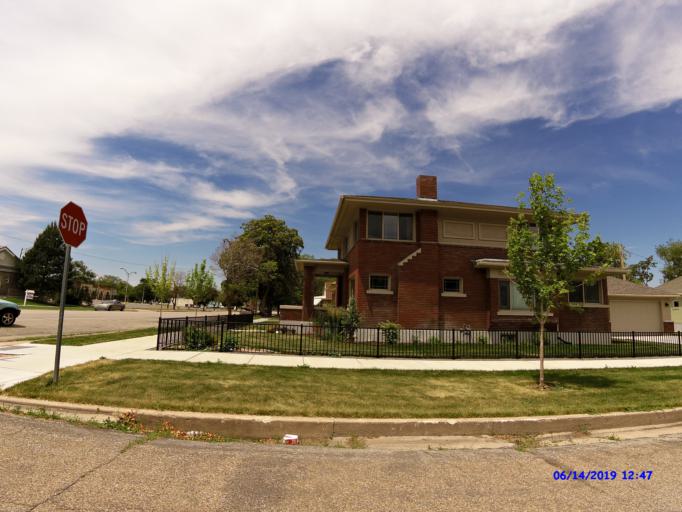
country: US
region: Utah
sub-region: Weber County
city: Ogden
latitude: 41.2227
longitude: -111.9565
